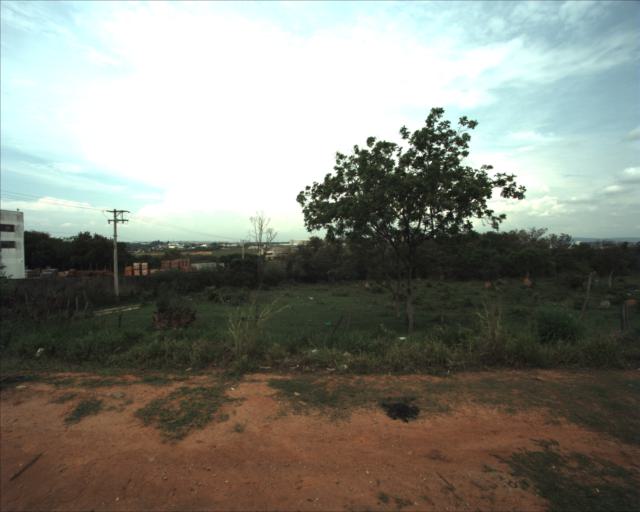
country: BR
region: Sao Paulo
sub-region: Sorocaba
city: Sorocaba
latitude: -23.4502
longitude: -47.4408
